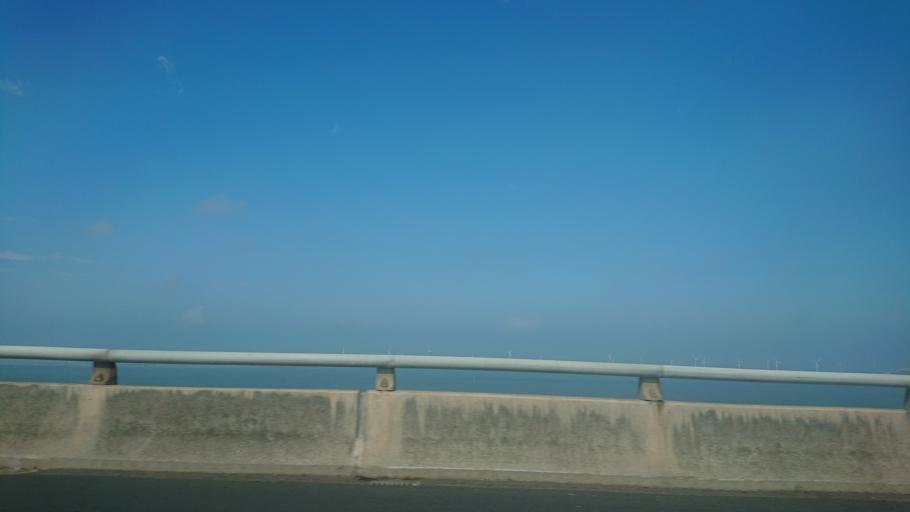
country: TW
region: Taiwan
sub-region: Changhua
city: Chang-hua
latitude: 24.0889
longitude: 120.4286
